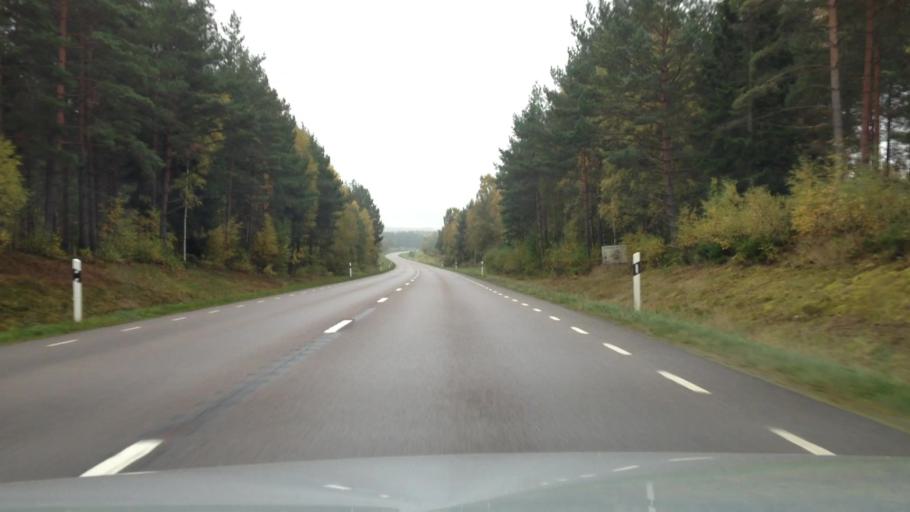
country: SE
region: Vaestra Goetaland
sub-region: Falkopings Kommun
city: Falkoeping
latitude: 58.2562
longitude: 13.5038
